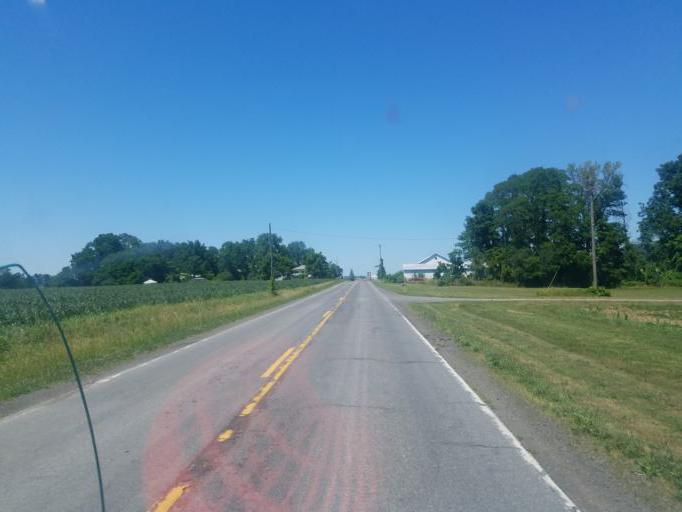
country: US
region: New York
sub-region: Yates County
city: Penn Yan
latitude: 42.7218
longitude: -76.9977
